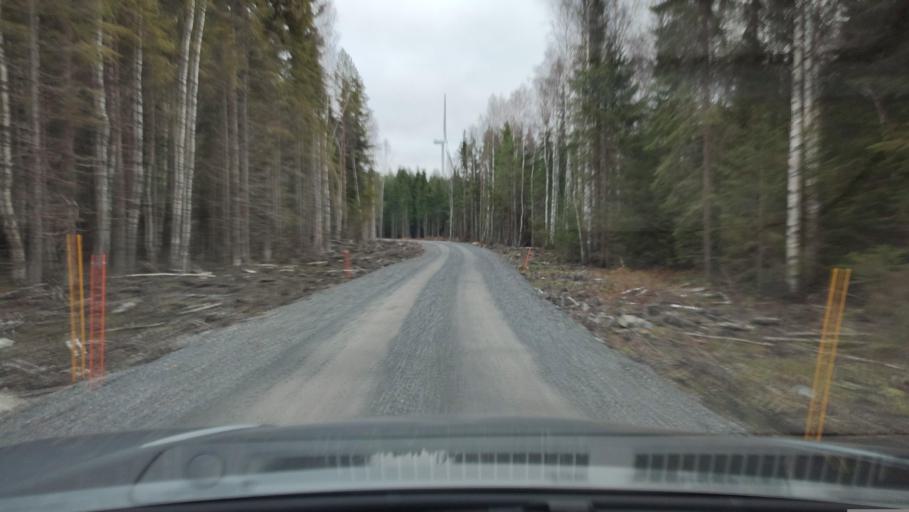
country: FI
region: Southern Ostrobothnia
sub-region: Suupohja
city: Karijoki
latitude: 62.1820
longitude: 21.5720
